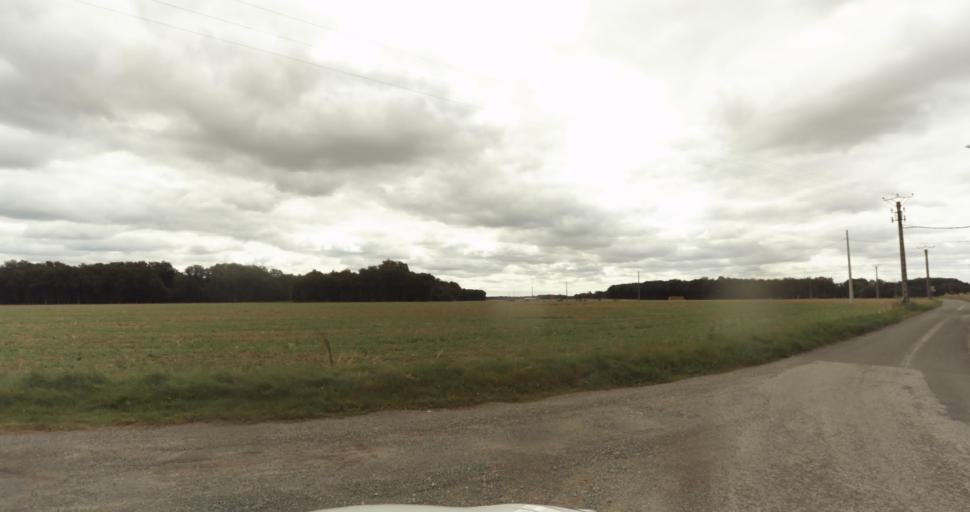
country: FR
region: Haute-Normandie
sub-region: Departement de l'Eure
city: La Madeleine-de-Nonancourt
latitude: 48.8187
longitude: 1.2167
